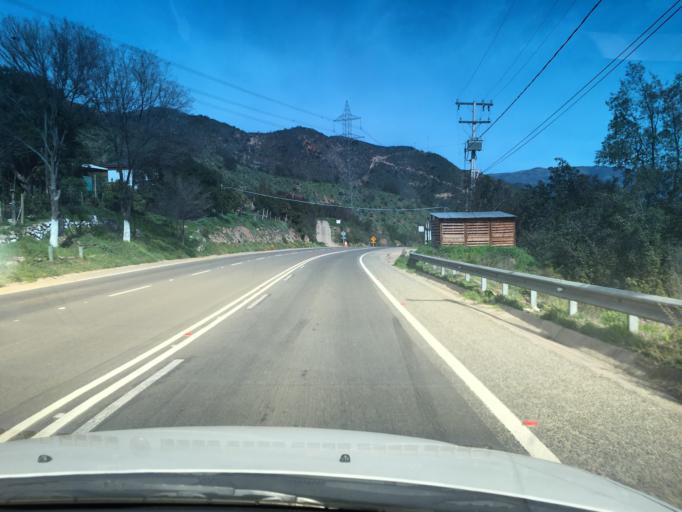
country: CL
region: Valparaiso
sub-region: Provincia de Marga Marga
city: Limache
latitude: -33.0587
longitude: -71.0468
